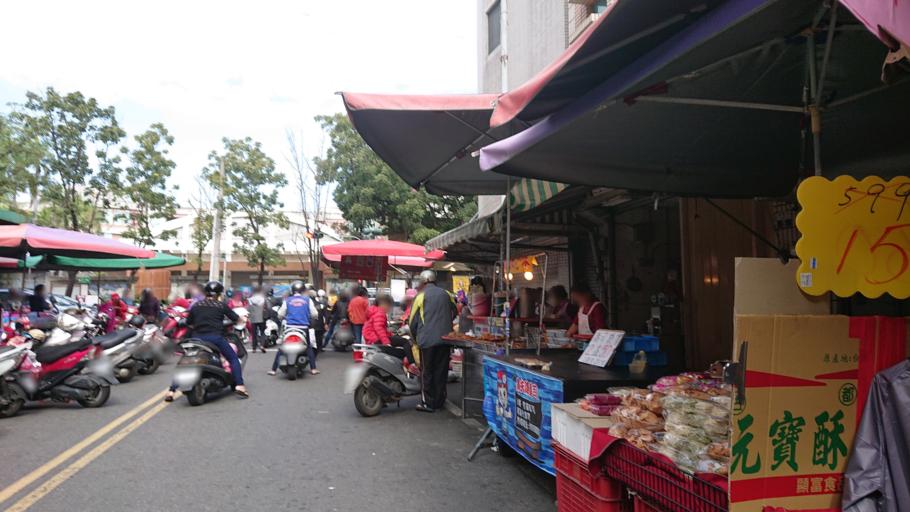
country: TW
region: Taiwan
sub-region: Tainan
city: Tainan
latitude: 23.0254
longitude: 120.2563
